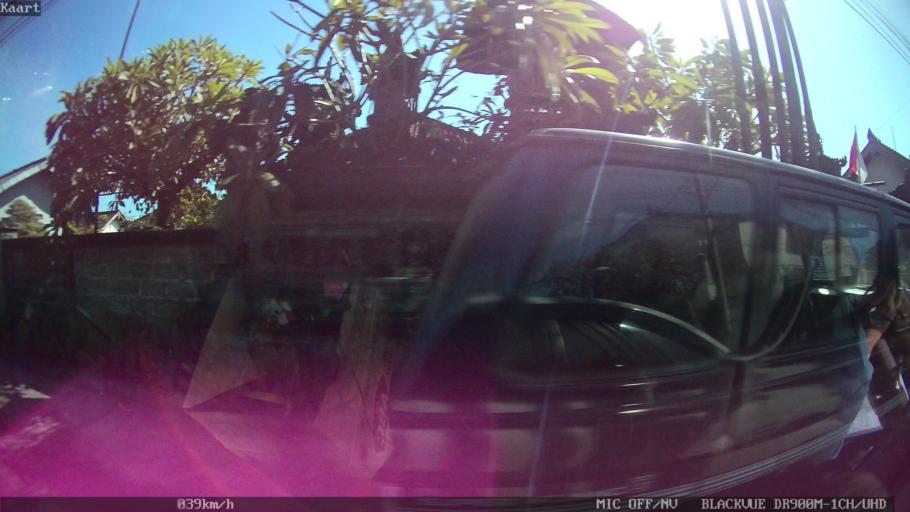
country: ID
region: Bali
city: Banjar Kertasari
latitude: -8.6291
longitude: 115.1870
